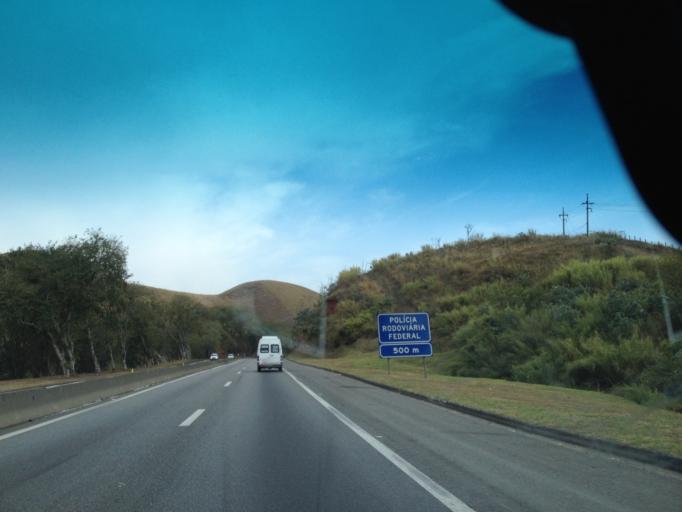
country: BR
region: Rio de Janeiro
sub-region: Porto Real
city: Porto Real
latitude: -22.4736
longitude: -44.2739
